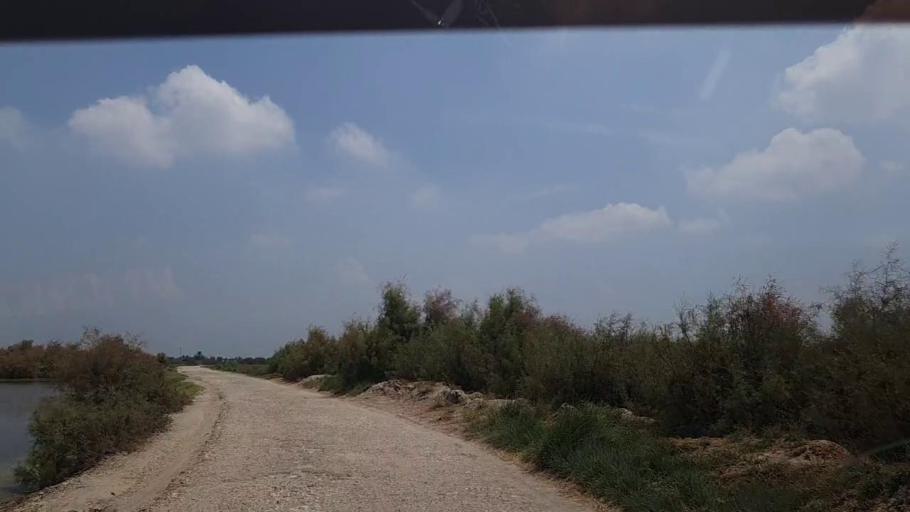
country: PK
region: Sindh
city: Khanpur
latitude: 27.8946
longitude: 69.3968
